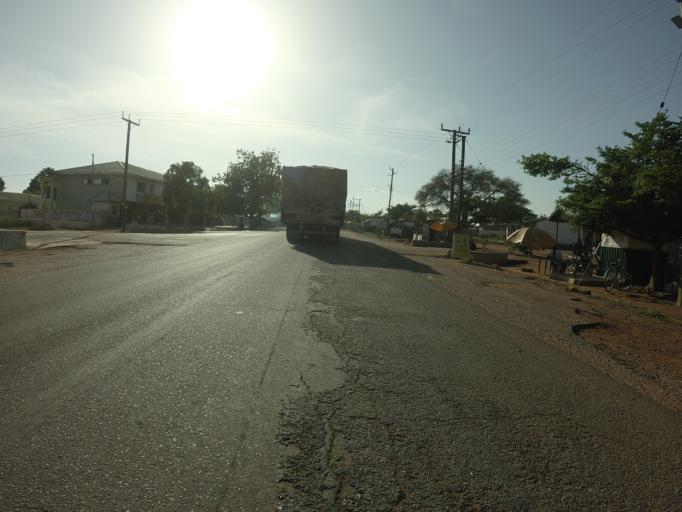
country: GH
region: Upper East
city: Navrongo
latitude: 10.8945
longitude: -1.0831
